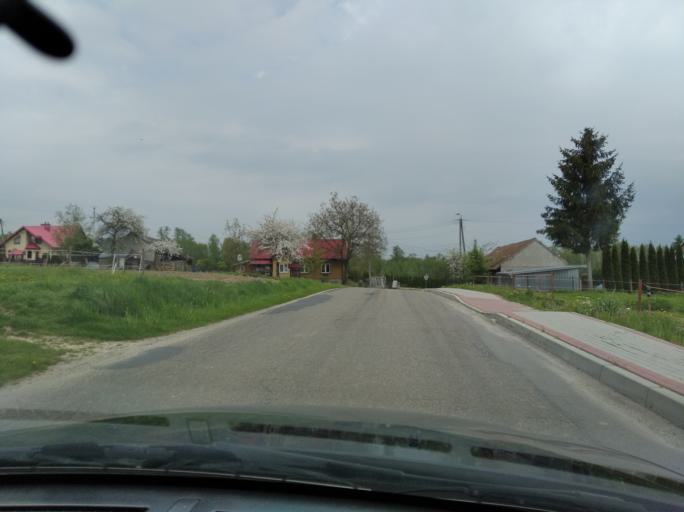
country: PL
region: Lesser Poland Voivodeship
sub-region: Powiat tarnowski
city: Skrzyszow
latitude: 49.9575
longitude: 21.0378
